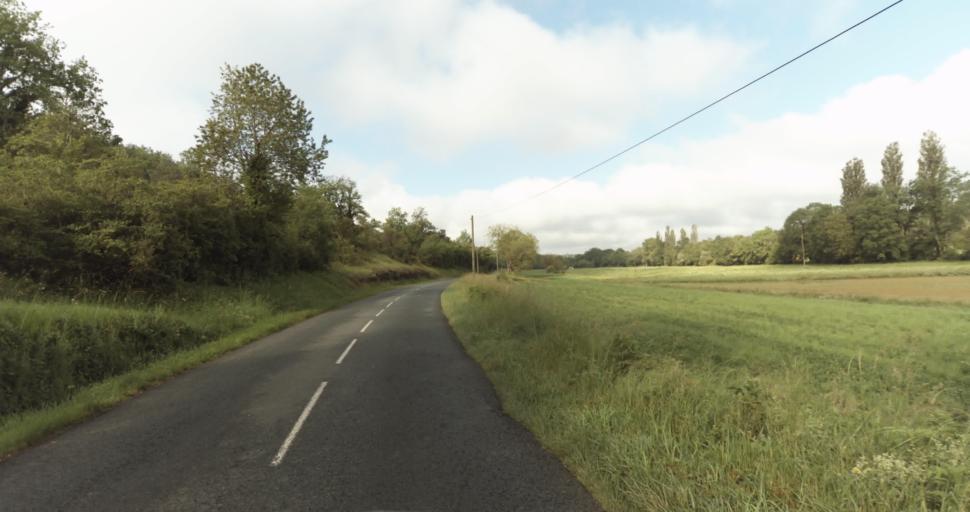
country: FR
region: Aquitaine
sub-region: Departement de la Dordogne
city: Lalinde
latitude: 44.9301
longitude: 0.7648
